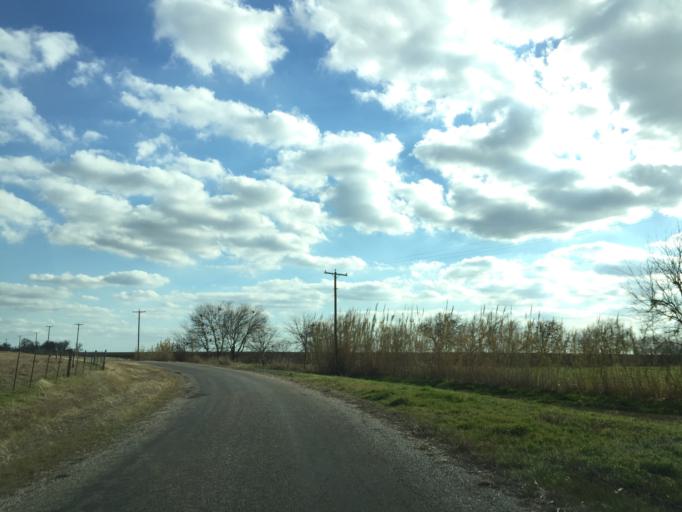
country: US
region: Texas
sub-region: Williamson County
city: Taylor
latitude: 30.6299
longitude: -97.4361
